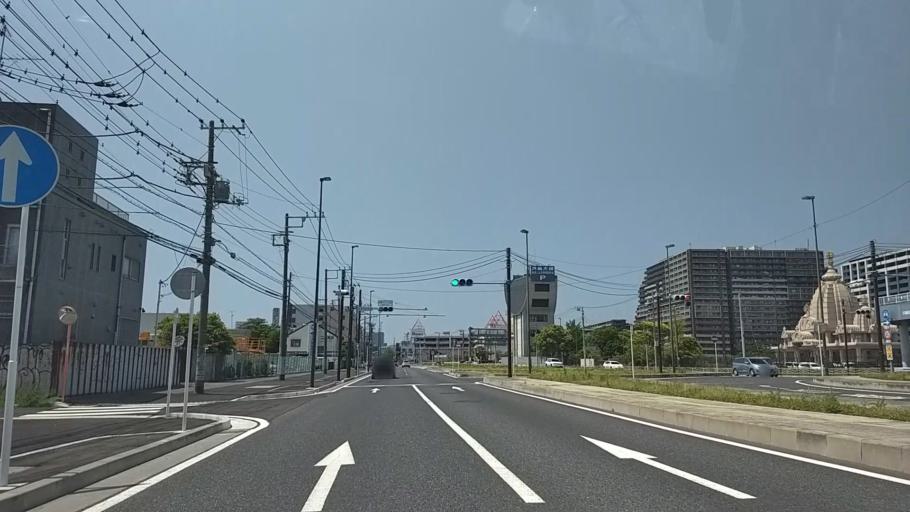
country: JP
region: Kanagawa
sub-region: Kawasaki-shi
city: Kawasaki
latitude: 35.5373
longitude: 139.7384
